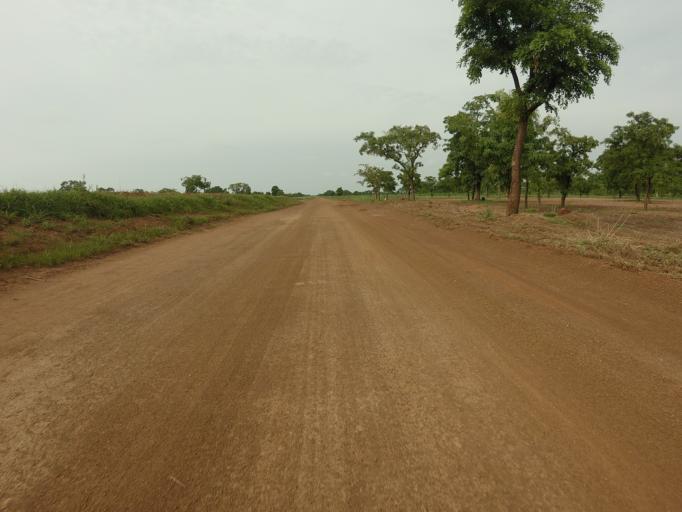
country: GH
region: Northern
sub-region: Yendi
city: Yendi
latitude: 9.7898
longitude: -0.1157
